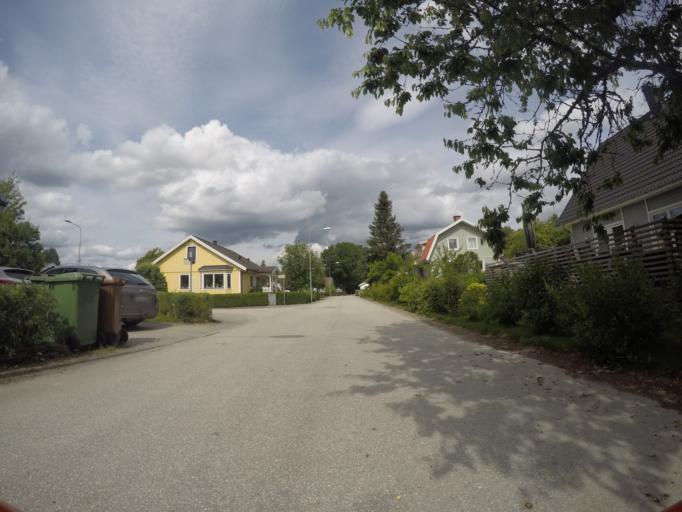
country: SE
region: Vaestra Goetaland
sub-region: Trollhattan
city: Trollhattan
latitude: 58.2294
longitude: 12.3046
